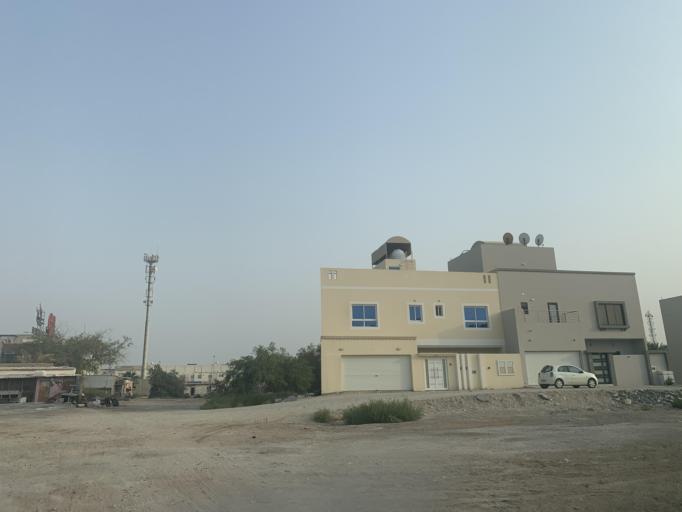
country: BH
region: Manama
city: Jidd Hafs
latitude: 26.2193
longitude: 50.5195
